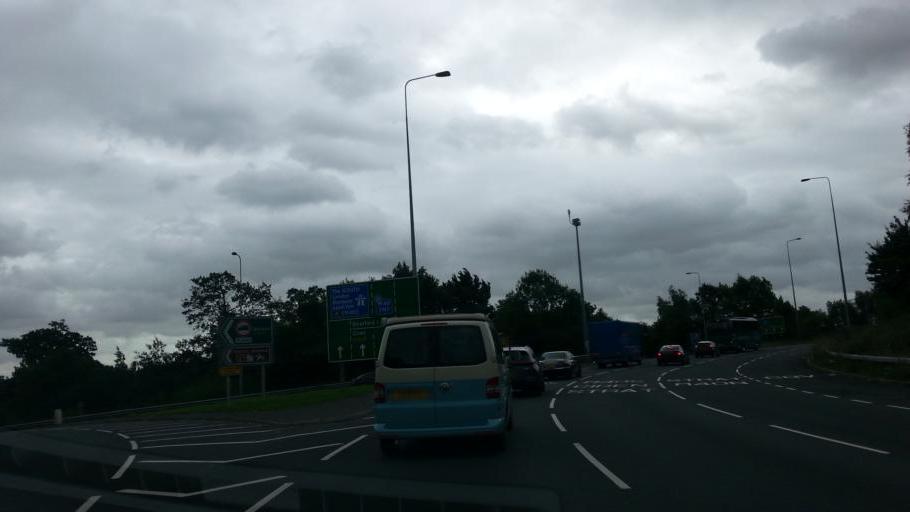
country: GB
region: England
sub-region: Warwickshire
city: Warwick
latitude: 52.2608
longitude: -1.6121
